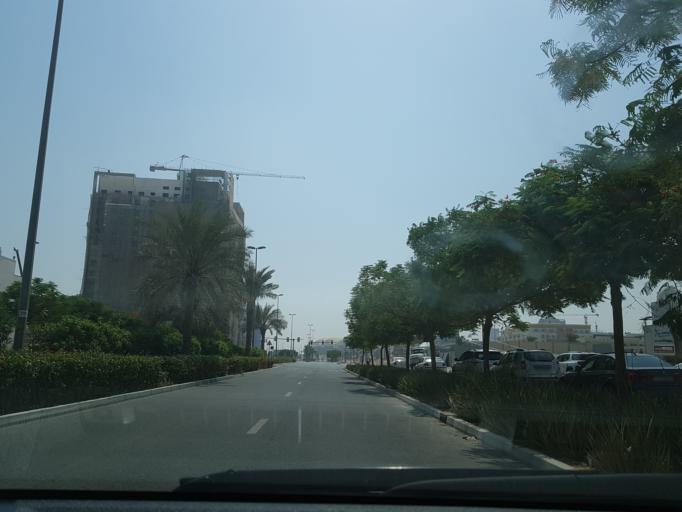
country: AE
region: Dubai
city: Dubai
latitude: 25.0547
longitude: 55.2103
